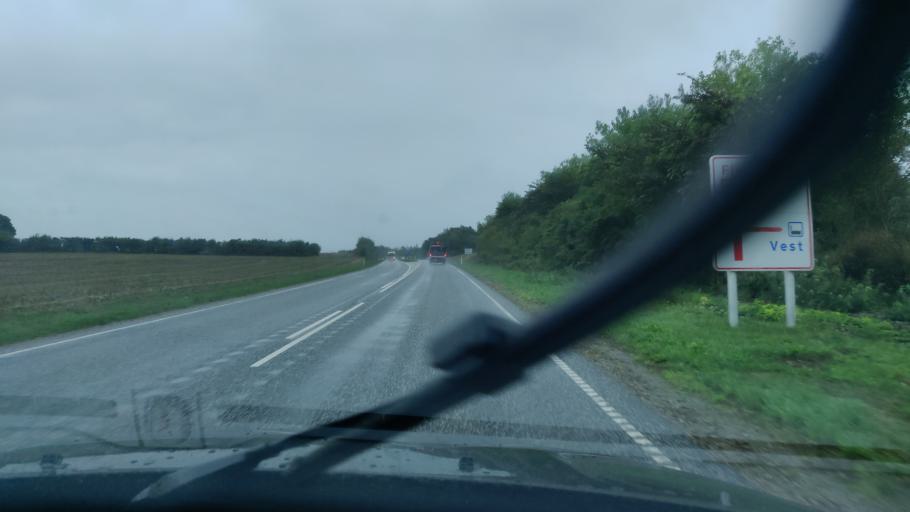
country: DK
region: North Denmark
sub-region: Thisted Kommune
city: Thisted
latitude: 56.9712
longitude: 8.7104
